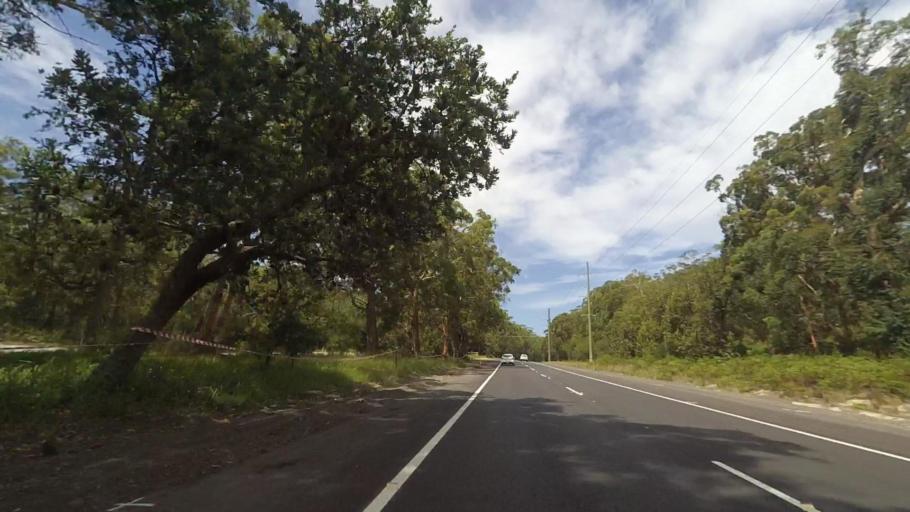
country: AU
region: New South Wales
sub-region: Port Stephens Shire
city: Anna Bay
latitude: -32.7802
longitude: 151.9874
